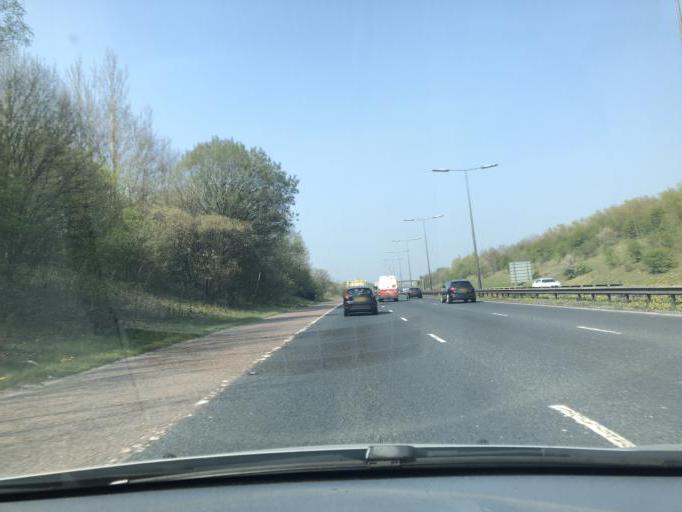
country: GB
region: England
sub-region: Borough of Tameside
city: Denton
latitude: 53.4438
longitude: -2.1332
